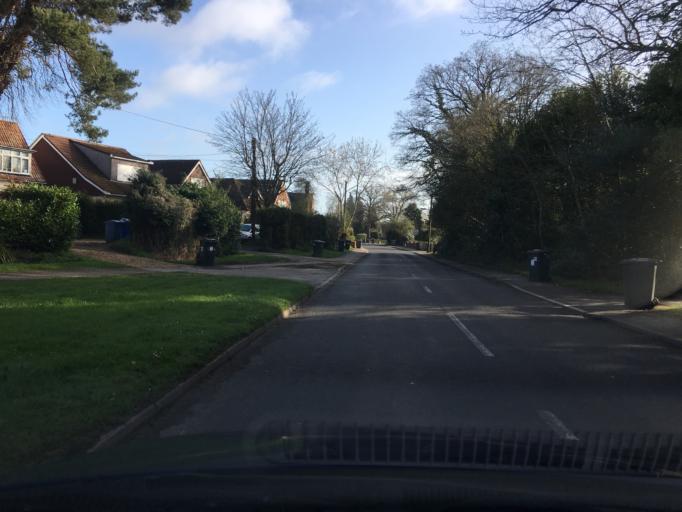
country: GB
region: England
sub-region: Bracknell Forest
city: Sandhurst
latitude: 51.3369
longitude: -0.8026
